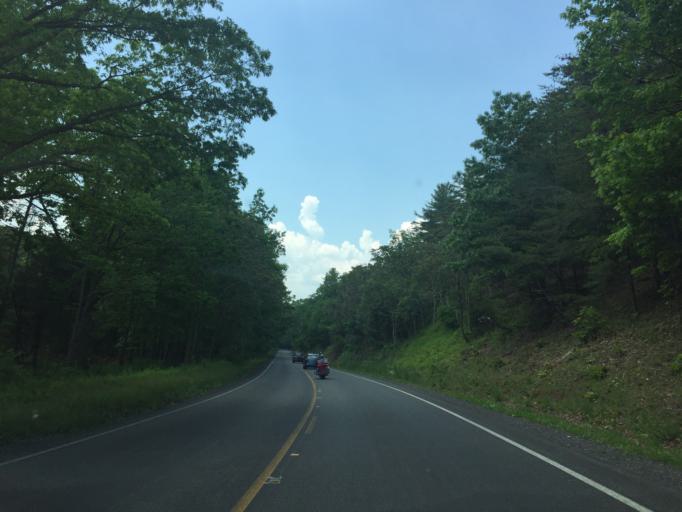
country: US
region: Virginia
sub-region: Shenandoah County
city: Woodstock
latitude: 39.0864
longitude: -78.5429
